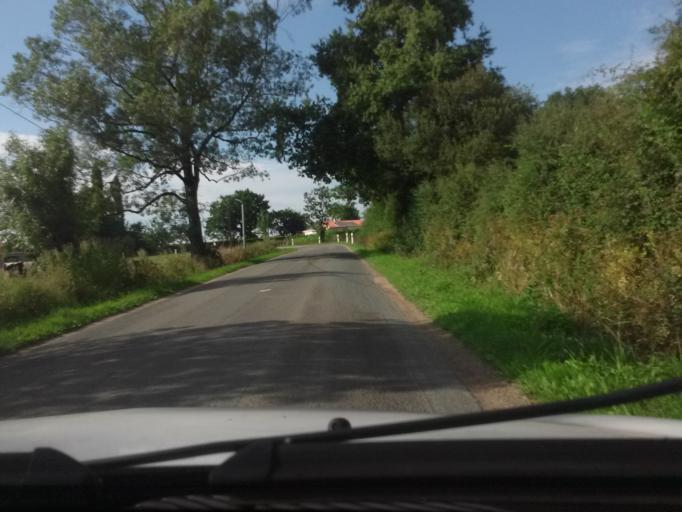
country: FR
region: Pays de la Loire
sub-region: Departement de la Vendee
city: La Bernardiere
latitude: 47.0344
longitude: -1.2367
